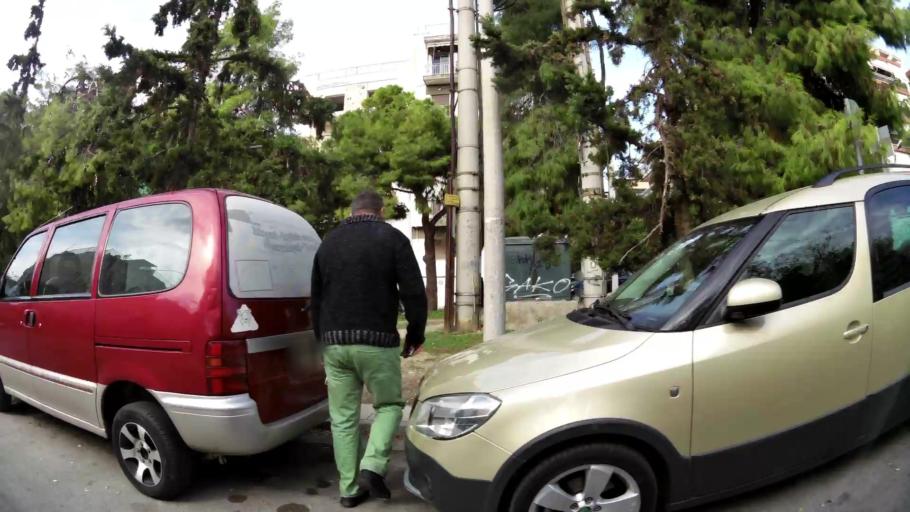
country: GR
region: Attica
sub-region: Nomarchia Athinas
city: Nea Smyrni
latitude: 37.9541
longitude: 23.7179
